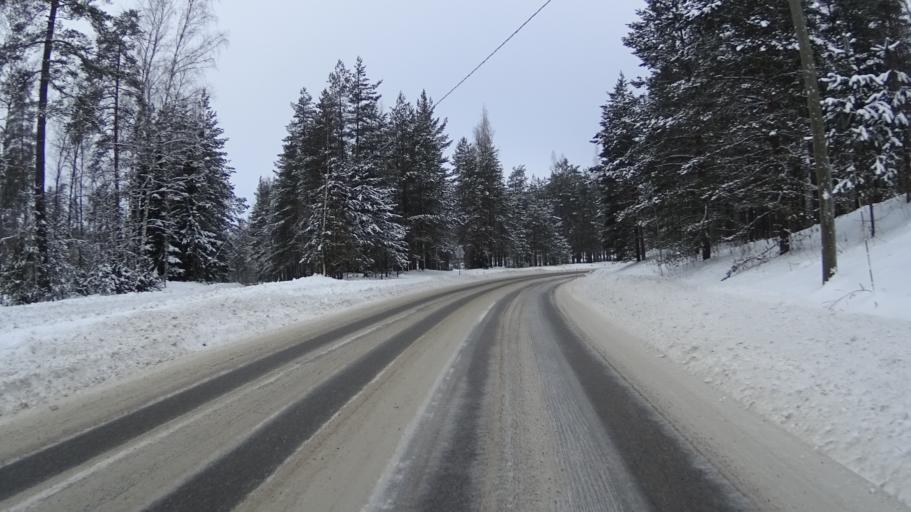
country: FI
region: Uusimaa
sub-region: Helsinki
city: Vihti
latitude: 60.3410
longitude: 24.3078
